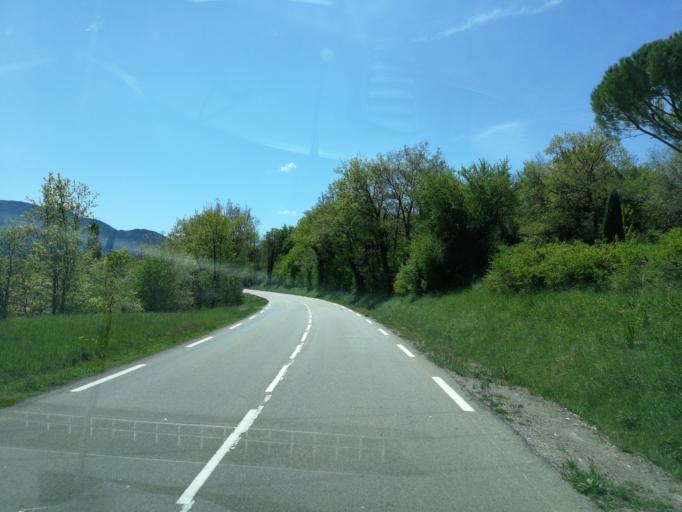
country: FR
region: Rhone-Alpes
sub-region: Departement de la Drome
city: Die
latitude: 44.7284
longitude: 5.2661
